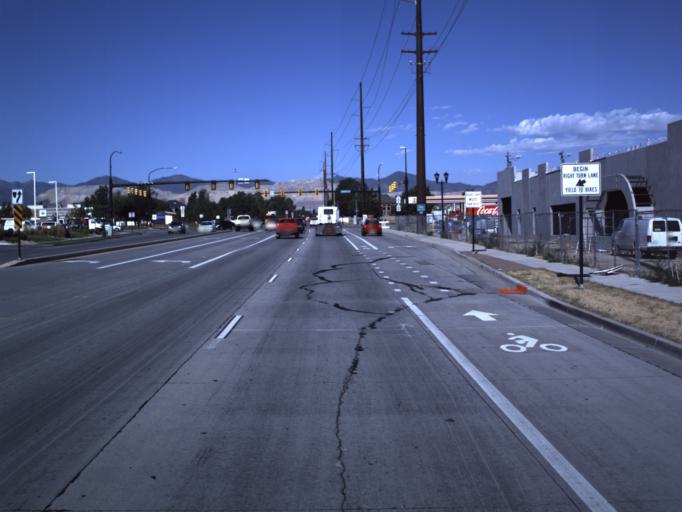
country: US
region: Utah
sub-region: Salt Lake County
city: South Jordan
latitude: 40.5443
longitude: -111.9370
